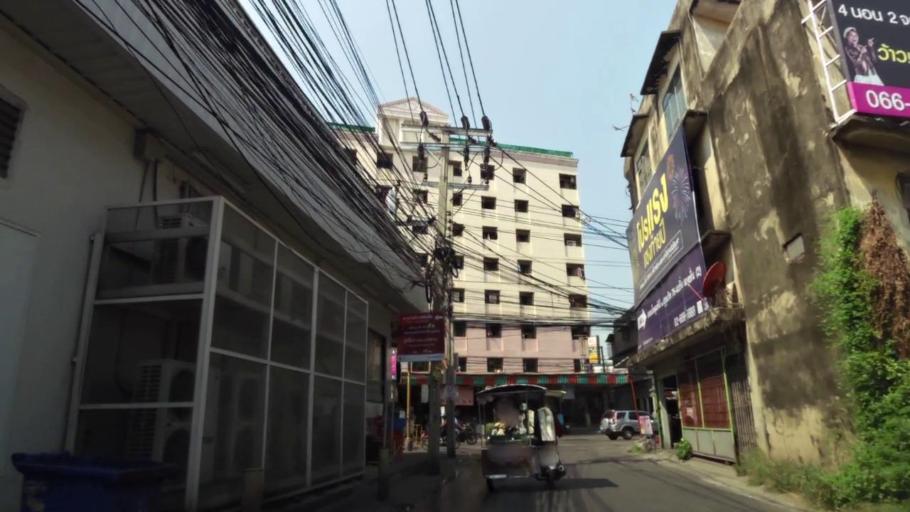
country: TH
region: Bangkok
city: Phra Khanong
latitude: 13.6553
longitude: 100.5932
